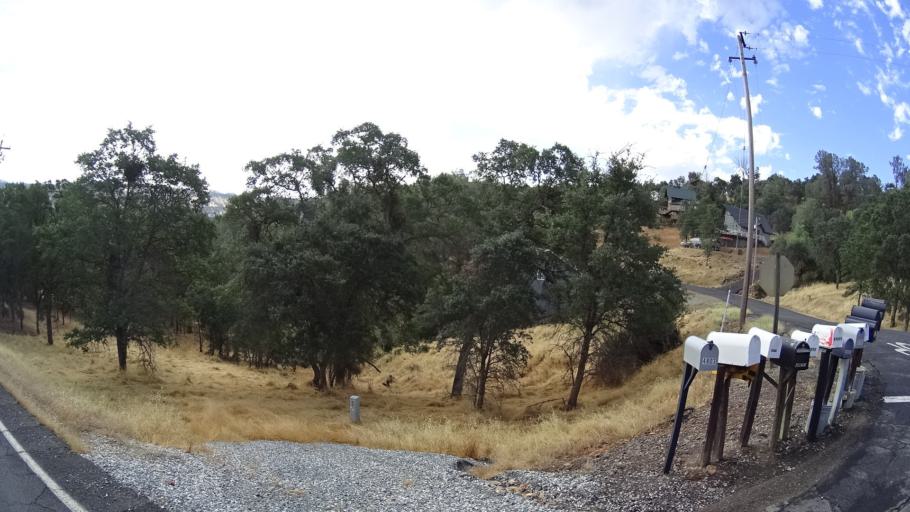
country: US
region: California
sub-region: Calaveras County
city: Copperopolis
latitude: 37.9102
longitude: -120.6073
